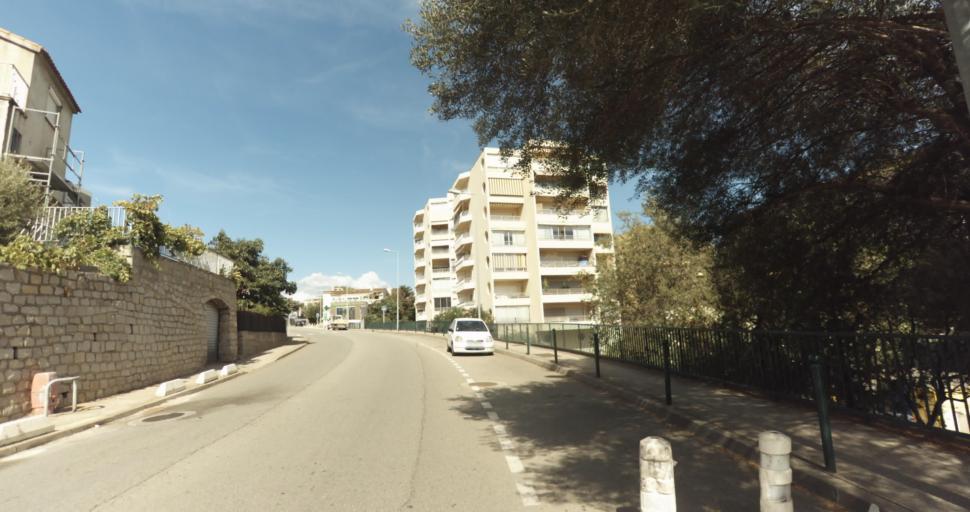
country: FR
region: Corsica
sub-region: Departement de la Corse-du-Sud
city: Ajaccio
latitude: 41.9349
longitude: 8.7558
